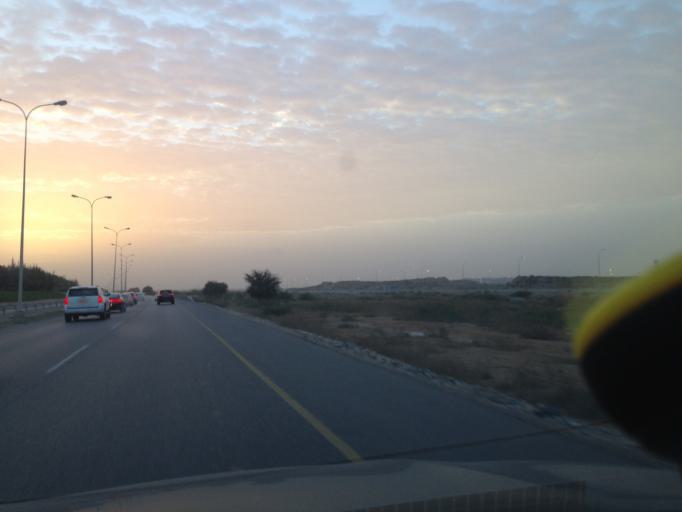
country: OM
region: Muhafazat Masqat
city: As Sib al Jadidah
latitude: 23.6202
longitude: 58.2735
